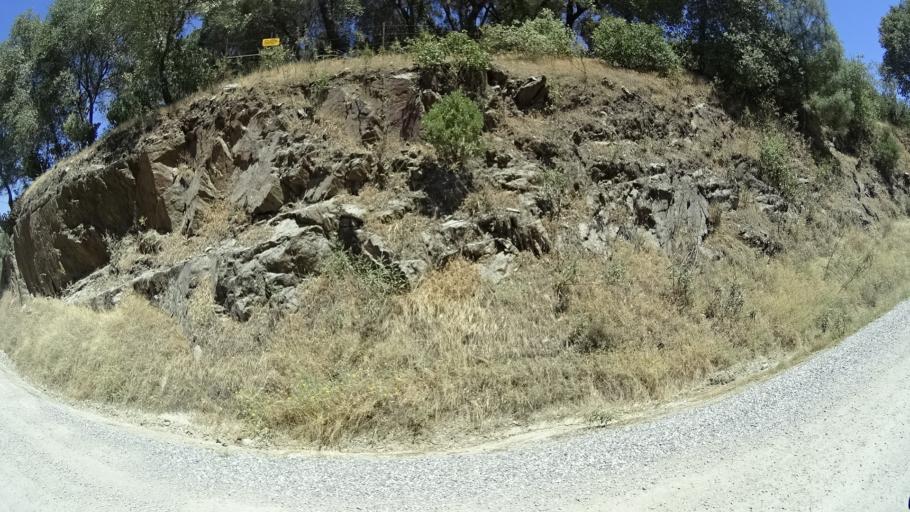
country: US
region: California
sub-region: Calaveras County
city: Murphys
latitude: 38.1066
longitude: -120.4942
